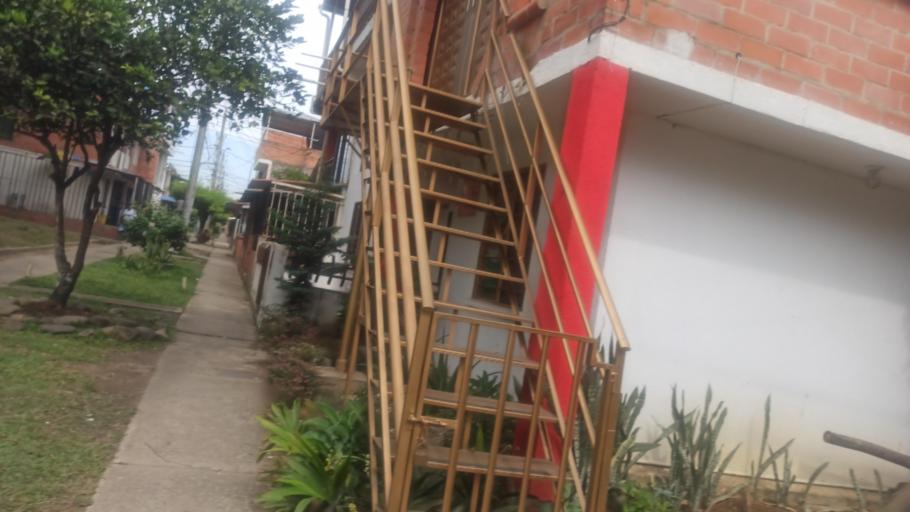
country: CO
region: Valle del Cauca
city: Jamundi
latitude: 3.2373
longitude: -76.5071
